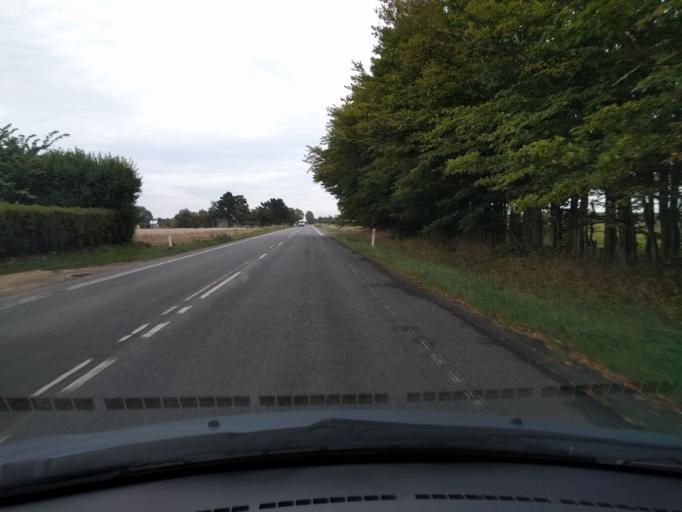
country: DK
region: Zealand
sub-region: Guldborgsund Kommune
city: Stubbekobing
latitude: 54.8937
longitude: 11.9871
